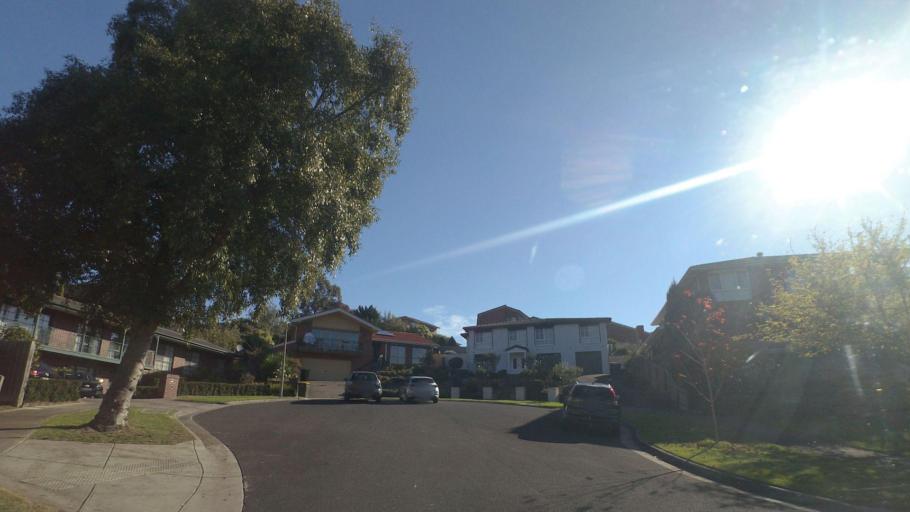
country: AU
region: Victoria
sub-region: Manningham
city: Doncaster East
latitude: -37.7663
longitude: 145.1621
